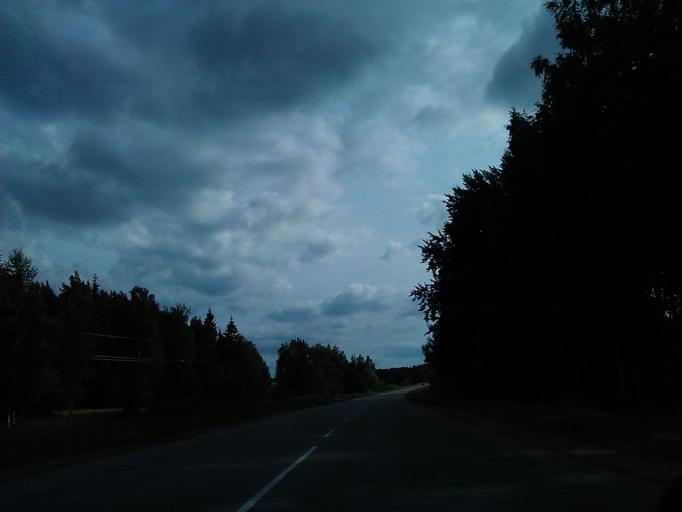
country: LV
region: Cesu Rajons
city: Cesis
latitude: 57.2918
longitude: 25.3030
